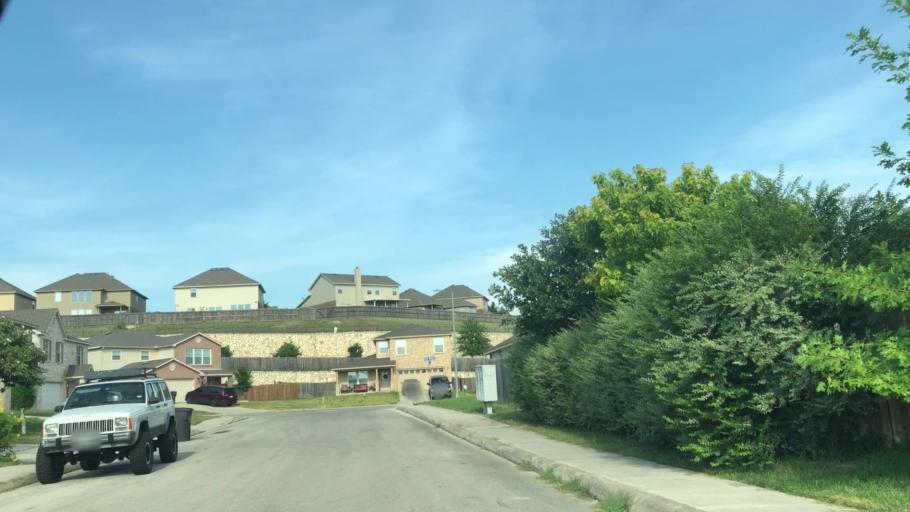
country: US
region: Texas
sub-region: Bexar County
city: Helotes
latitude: 29.5562
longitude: -98.6512
